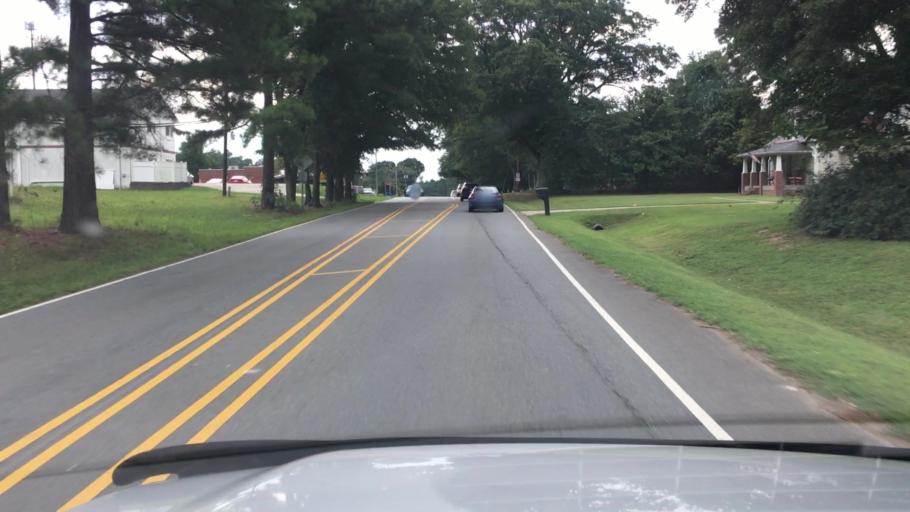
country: US
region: North Carolina
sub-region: Mecklenburg County
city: Huntersville
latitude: 35.3526
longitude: -80.8887
